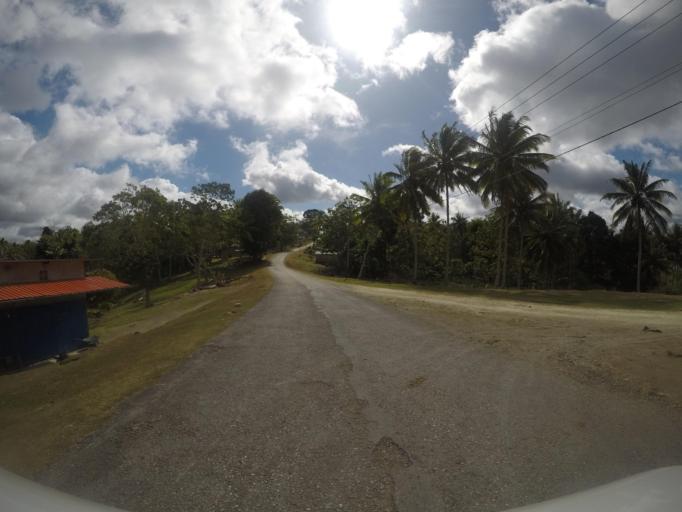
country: TL
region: Lautem
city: Lospalos
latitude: -8.5333
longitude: 126.9283
